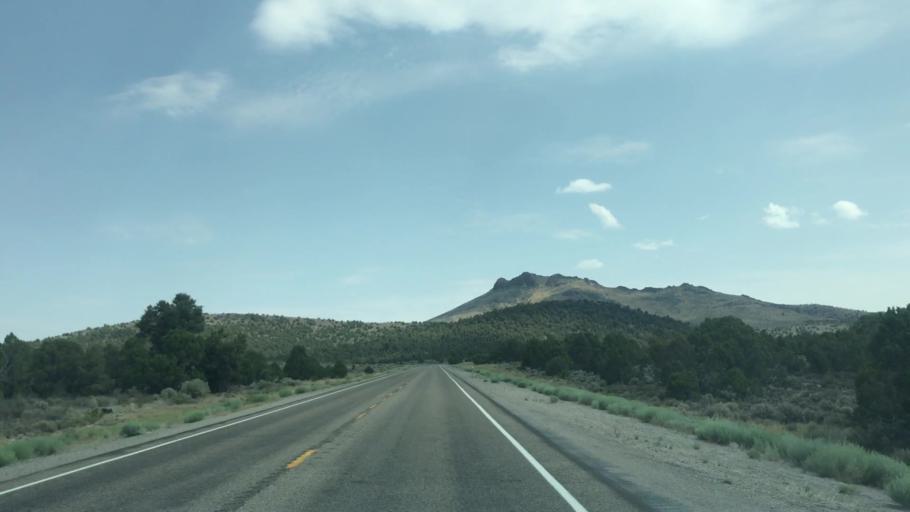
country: US
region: Nevada
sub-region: White Pine County
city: Ely
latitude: 39.4053
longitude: -115.0808
